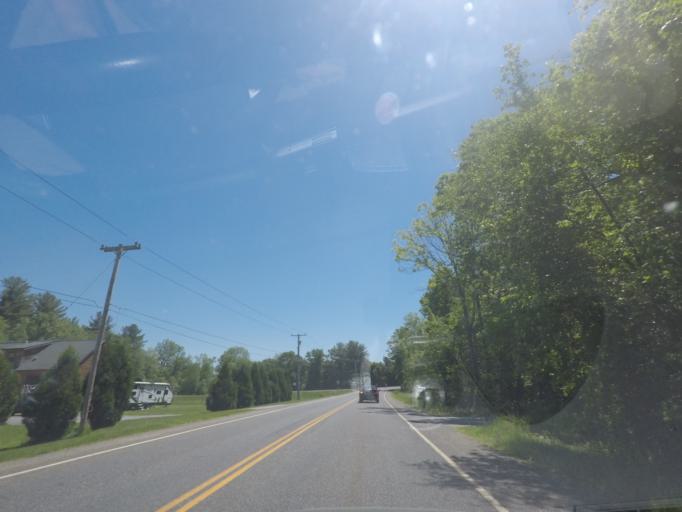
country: US
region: New York
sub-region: Saratoga County
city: Mechanicville
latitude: 42.9453
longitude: -73.7102
